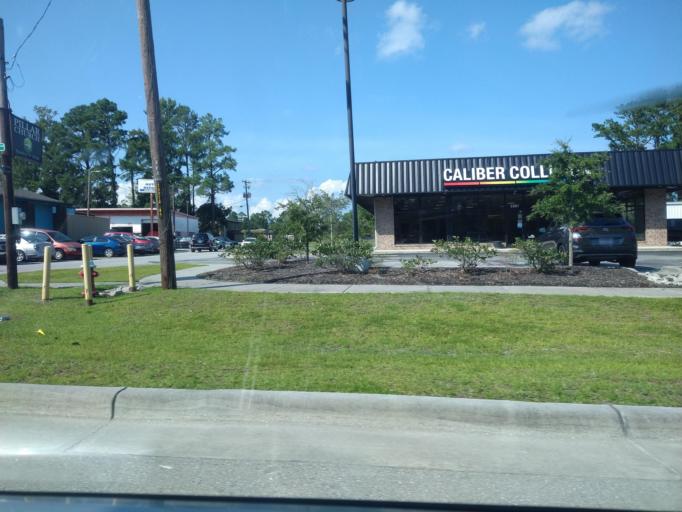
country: US
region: North Carolina
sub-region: Onslow County
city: Piney Green
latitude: 34.7389
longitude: -77.3601
